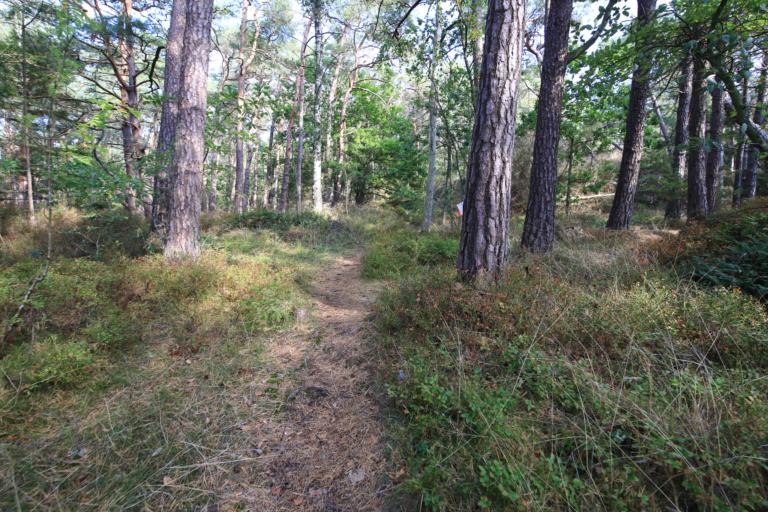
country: SE
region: Halland
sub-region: Varbergs Kommun
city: Varberg
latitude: 57.1734
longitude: 12.2063
